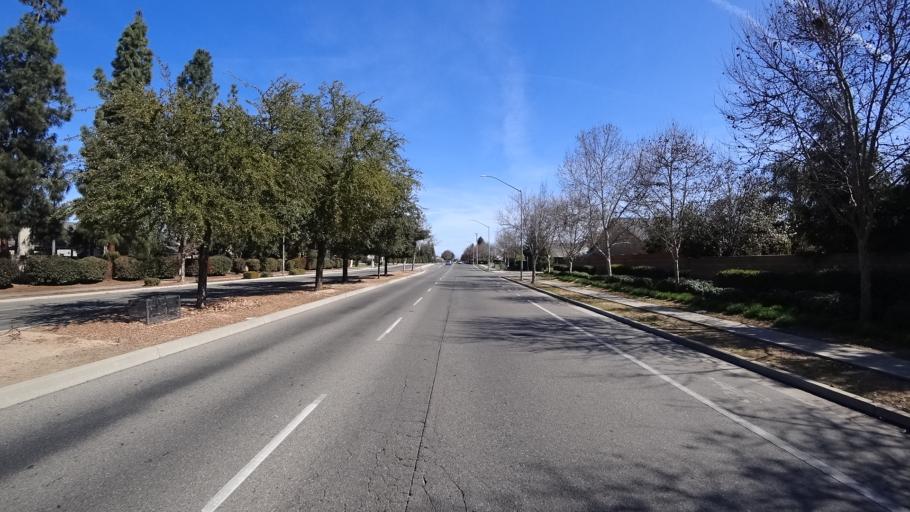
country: US
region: California
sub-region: Fresno County
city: Clovis
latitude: 36.8520
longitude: -119.7450
